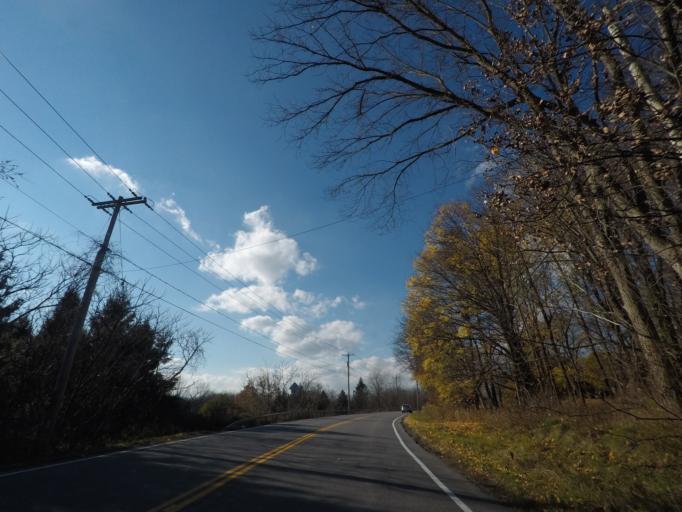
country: US
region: New York
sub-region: Saratoga County
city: Country Knolls
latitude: 42.8923
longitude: -73.8632
